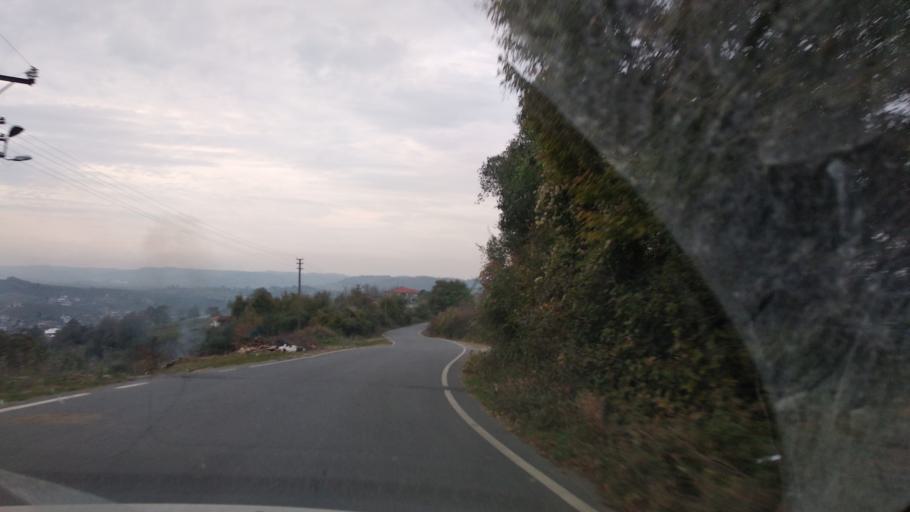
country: TR
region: Sakarya
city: Ortakoy
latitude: 41.0356
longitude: 30.6573
